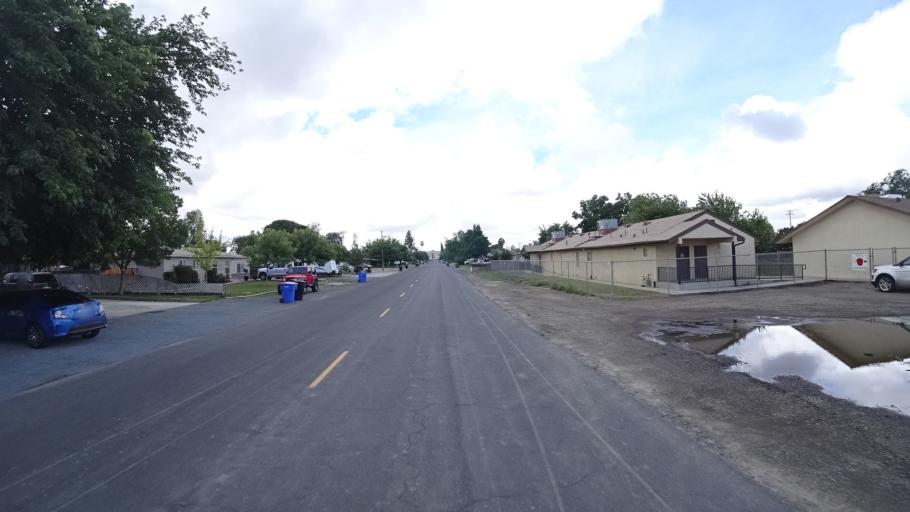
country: US
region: California
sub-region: Kings County
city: Hanford
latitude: 36.3416
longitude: -119.6715
